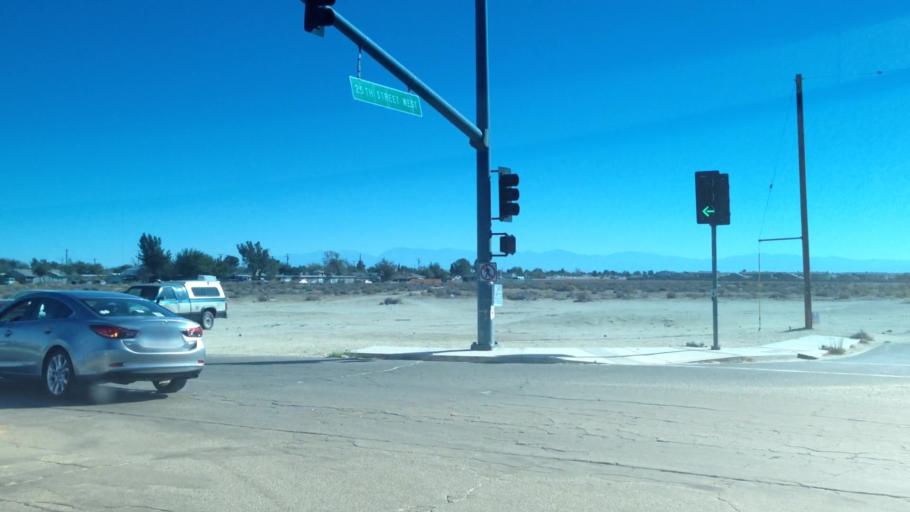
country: US
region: California
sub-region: Kern County
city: Rosamond
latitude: 34.8642
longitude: -118.1759
